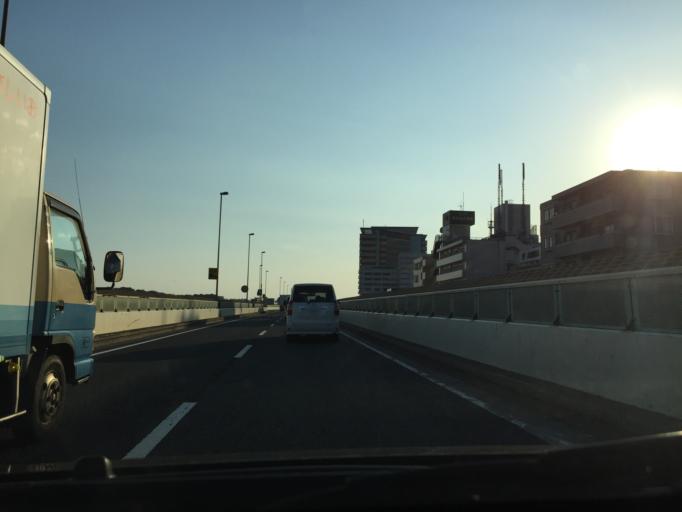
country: JP
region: Kanagawa
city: Yokohama
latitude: 35.4348
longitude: 139.6303
